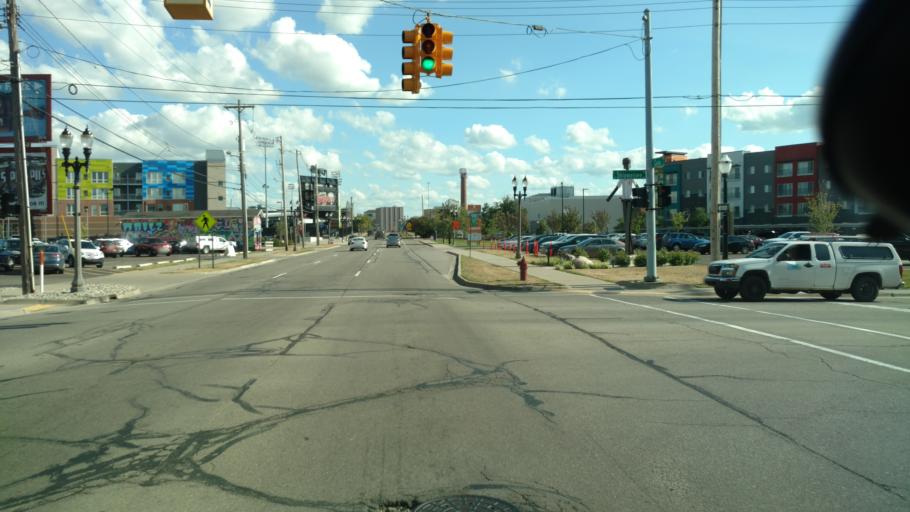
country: US
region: Michigan
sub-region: Ingham County
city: Lansing
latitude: 42.7372
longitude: -84.5466
